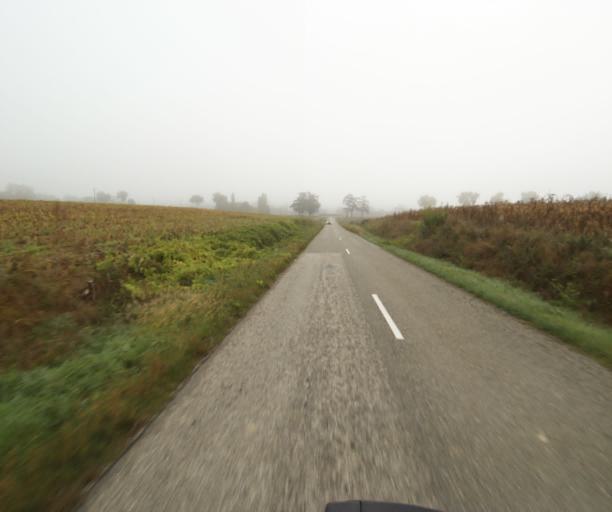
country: FR
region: Midi-Pyrenees
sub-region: Departement du Tarn-et-Garonne
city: Saint-Nauphary
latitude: 43.9416
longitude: 1.4622
